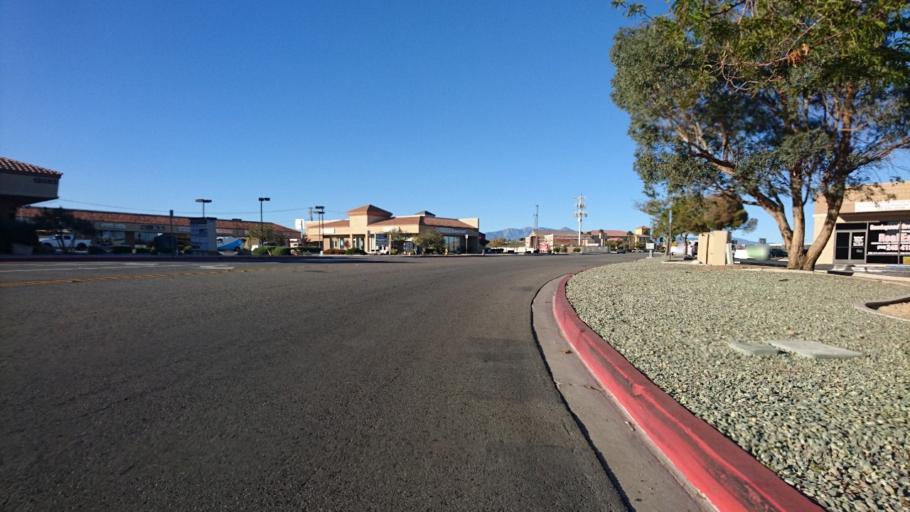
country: US
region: California
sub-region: San Bernardino County
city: Mountain View Acres
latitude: 34.4700
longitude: -117.3432
